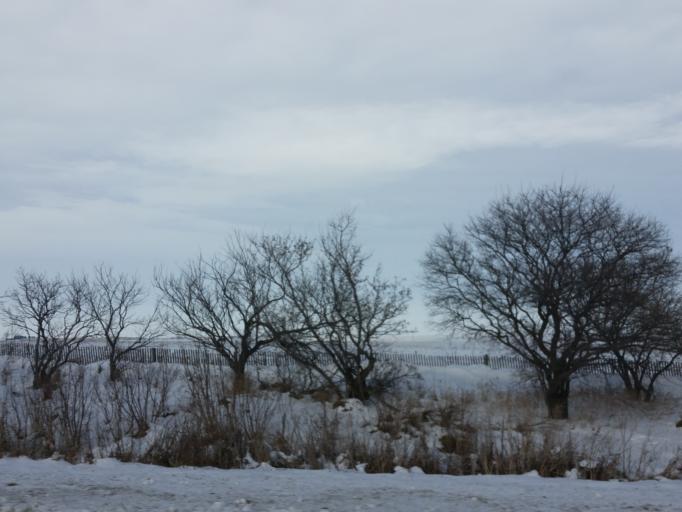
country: US
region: Iowa
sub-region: Delaware County
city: Manchester
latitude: 42.4642
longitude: -91.6378
